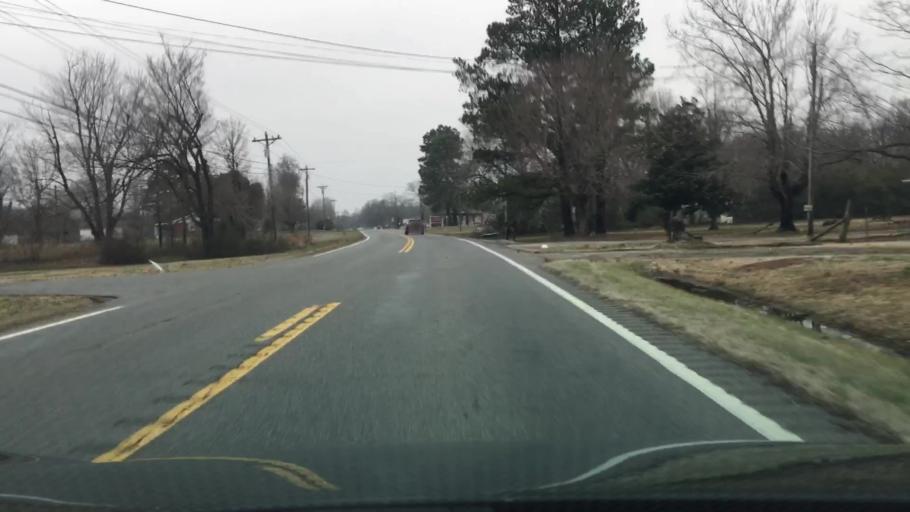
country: US
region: Kentucky
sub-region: Marshall County
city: Calvert City
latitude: 36.9716
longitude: -88.3926
